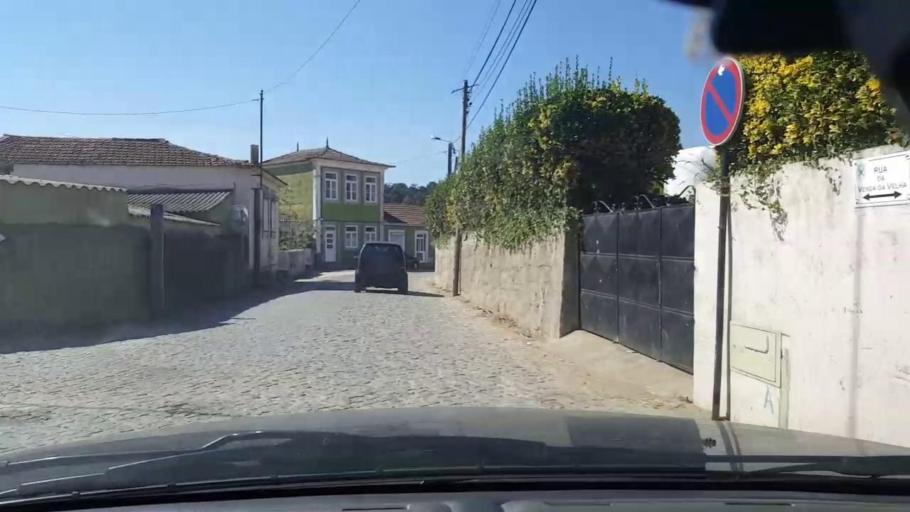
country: PT
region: Porto
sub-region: Matosinhos
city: Lavra
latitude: 41.2725
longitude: -8.6935
